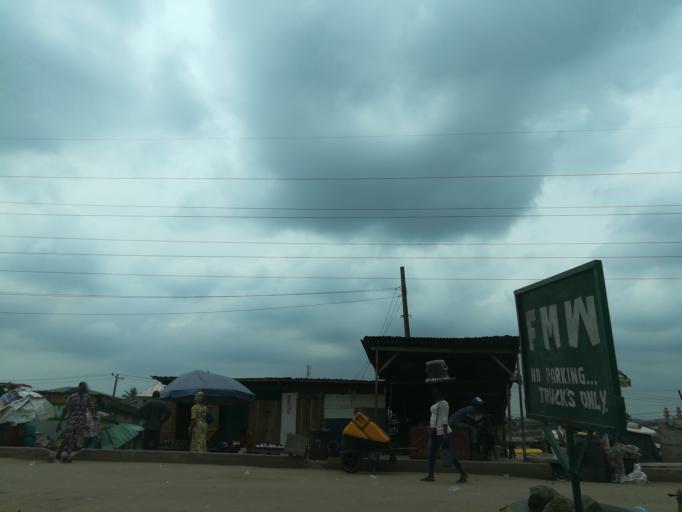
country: NG
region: Lagos
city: Ojota
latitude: 6.6115
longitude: 3.4130
